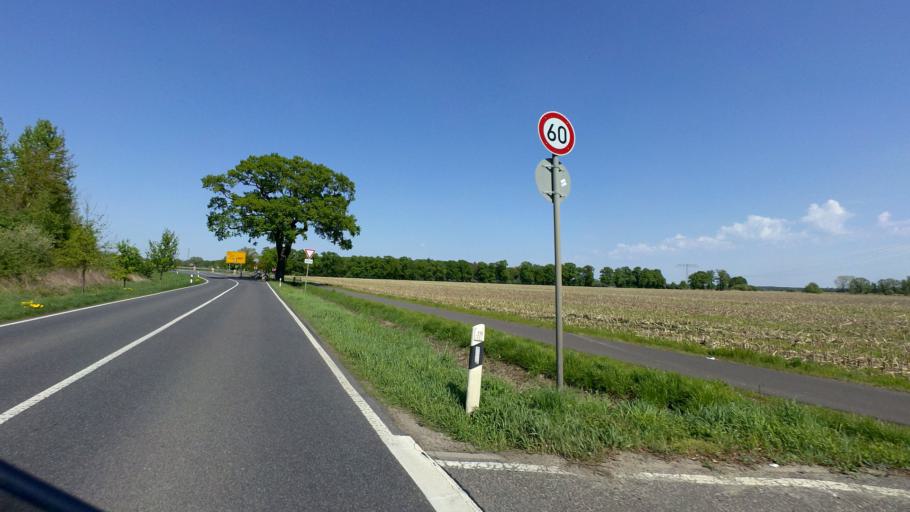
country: DE
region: Brandenburg
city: Beeskow
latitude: 52.1889
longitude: 14.2897
